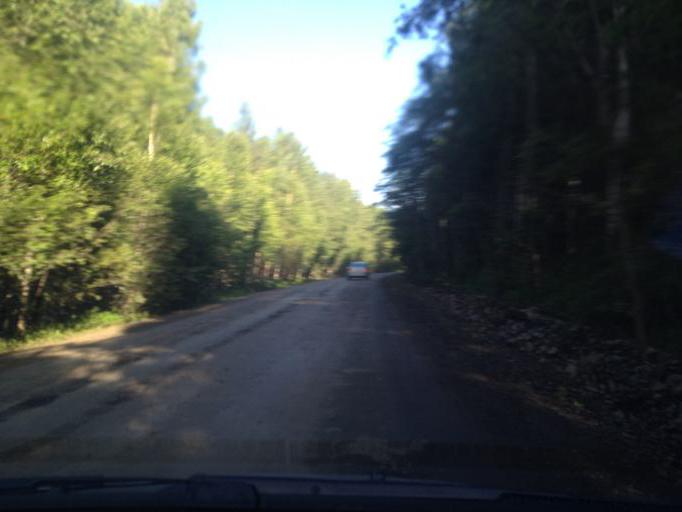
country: RU
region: Chelyabinsk
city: Cheremshanka
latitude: 56.2106
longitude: 60.4401
